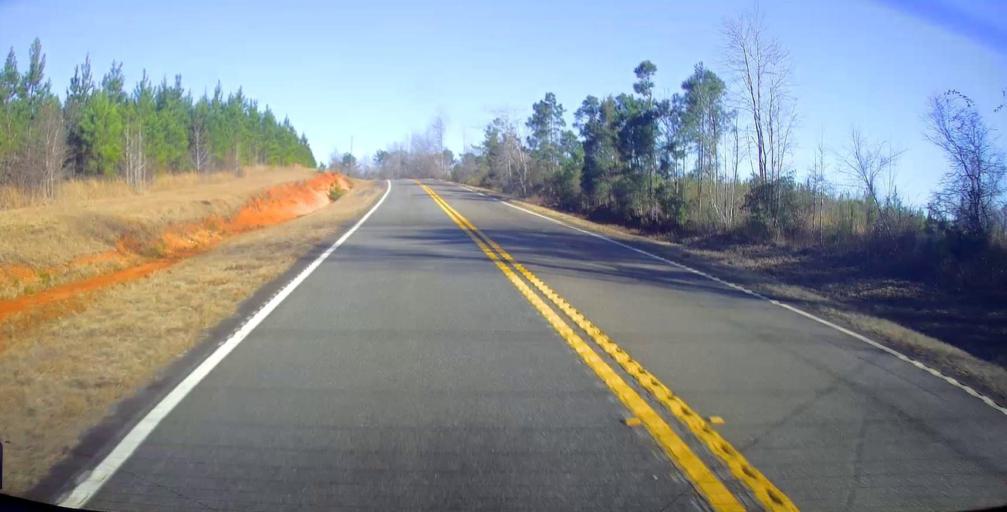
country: US
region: Georgia
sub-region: Talbot County
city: Talbotton
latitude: 32.6516
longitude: -84.4542
